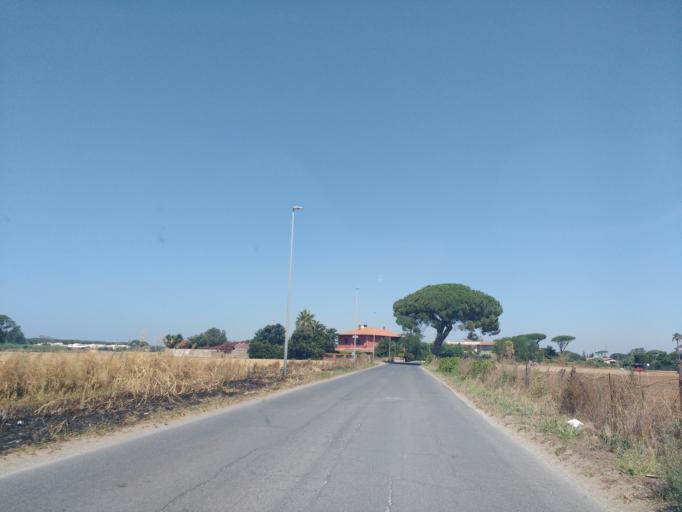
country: IT
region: Latium
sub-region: Citta metropolitana di Roma Capitale
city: Fregene
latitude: 41.8497
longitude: 12.2188
